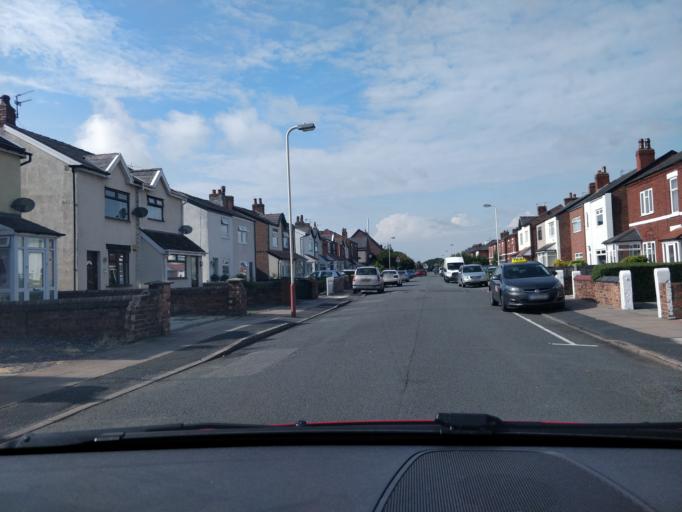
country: GB
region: England
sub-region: Sefton
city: Southport
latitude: 53.6492
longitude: -2.9634
